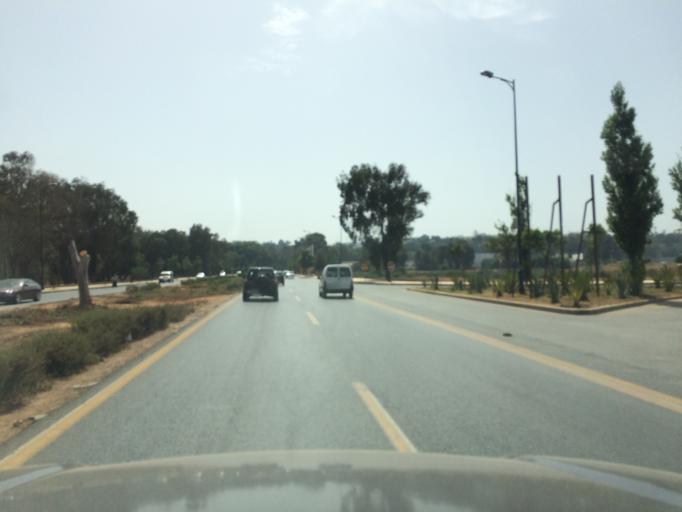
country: MA
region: Rabat-Sale-Zemmour-Zaer
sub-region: Rabat
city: Rabat
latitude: 34.0191
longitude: -6.8117
